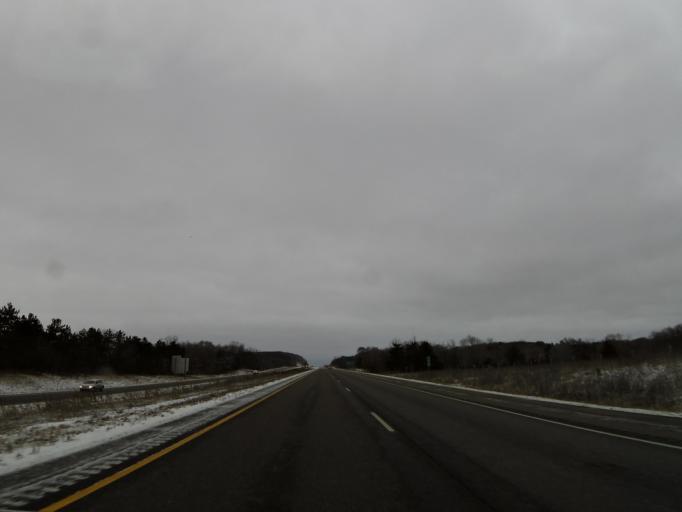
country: US
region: Wisconsin
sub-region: Eau Claire County
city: Eau Claire
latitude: 44.7885
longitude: -91.5462
